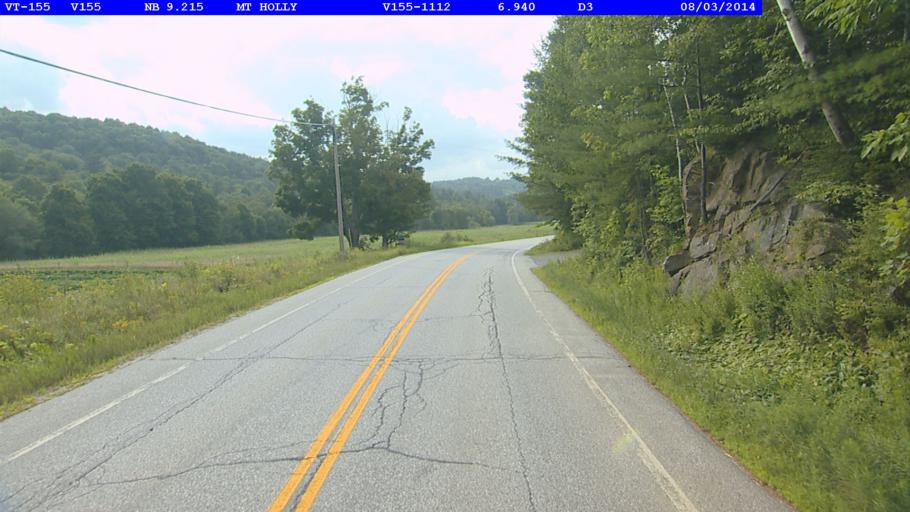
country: US
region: Vermont
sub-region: Rutland County
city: Rutland
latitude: 43.4408
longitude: -72.8648
